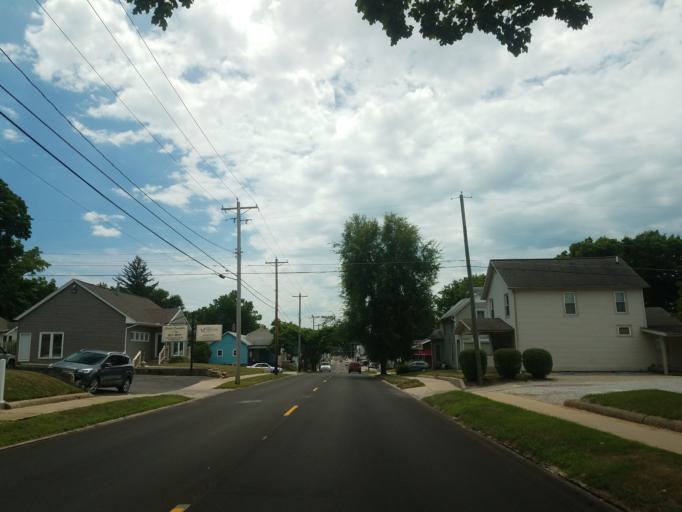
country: US
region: Illinois
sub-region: McLean County
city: Bloomington
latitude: 40.4828
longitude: -88.9848
